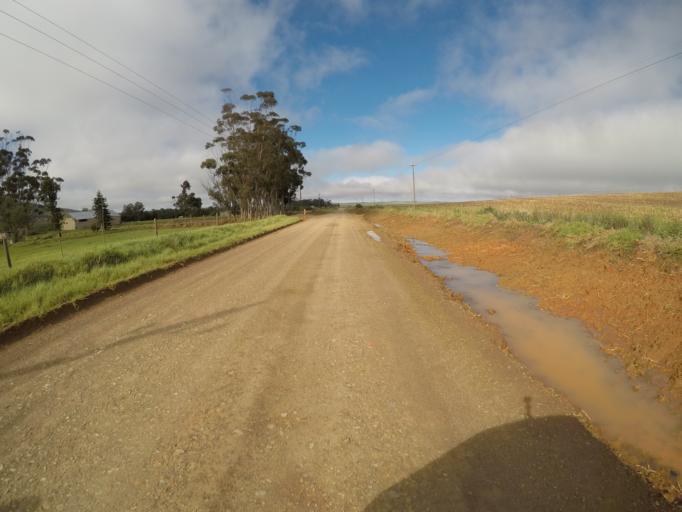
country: ZA
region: Western Cape
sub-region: Cape Winelands District Municipality
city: Ashton
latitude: -34.1333
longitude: 19.8561
